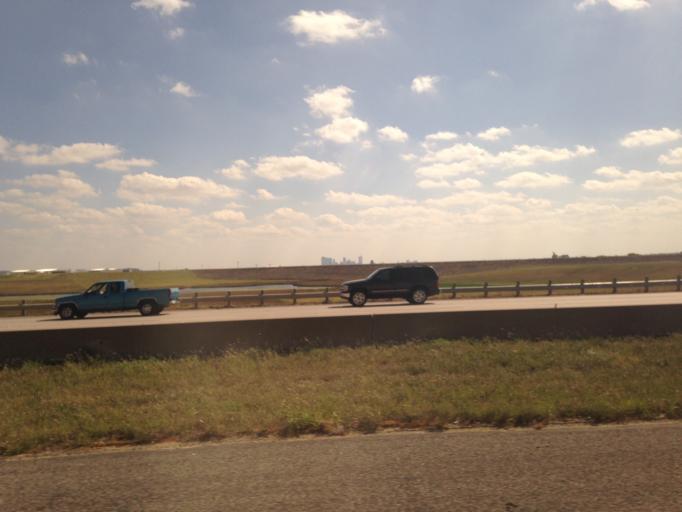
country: US
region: Texas
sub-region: Tarrant County
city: Saginaw
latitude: 32.8344
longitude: -97.3690
